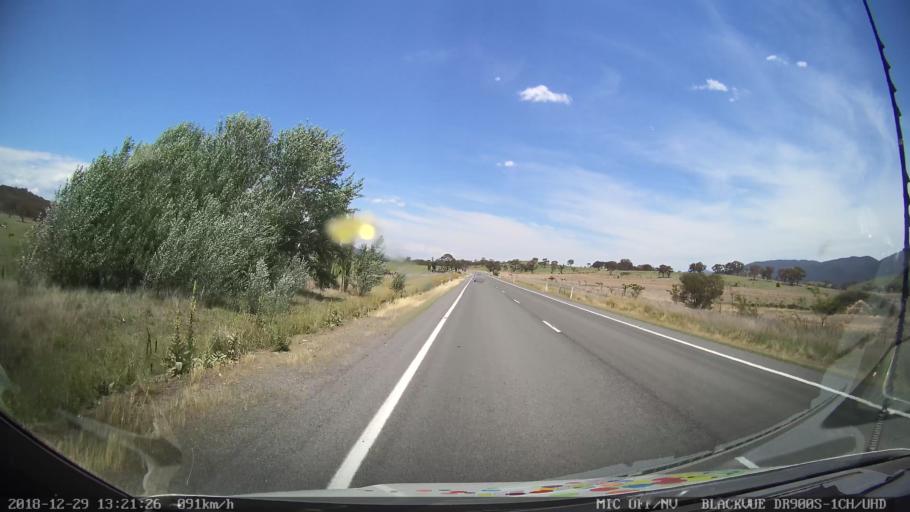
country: AU
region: Australian Capital Territory
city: Macarthur
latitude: -35.7922
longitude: 149.1639
